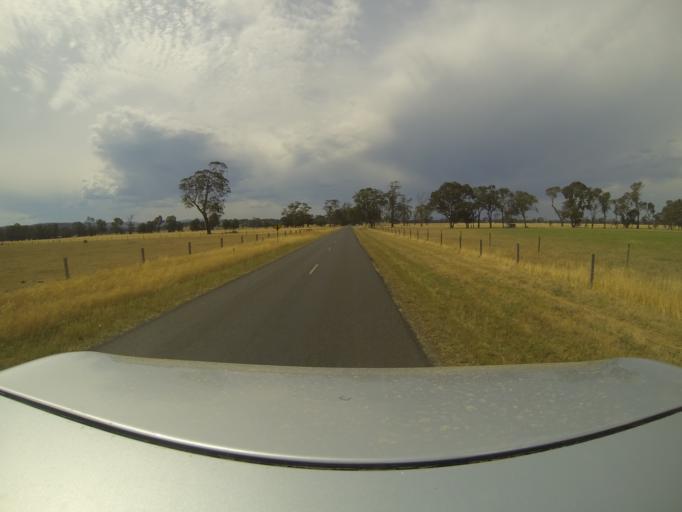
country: AU
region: Victoria
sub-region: Wellington
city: Heyfield
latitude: -37.9814
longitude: 146.6946
